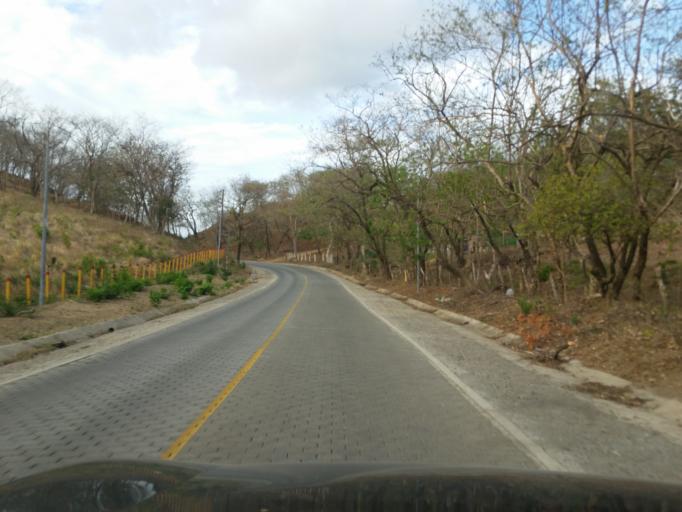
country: NI
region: Rivas
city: Tola
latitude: 11.4094
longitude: -85.9548
